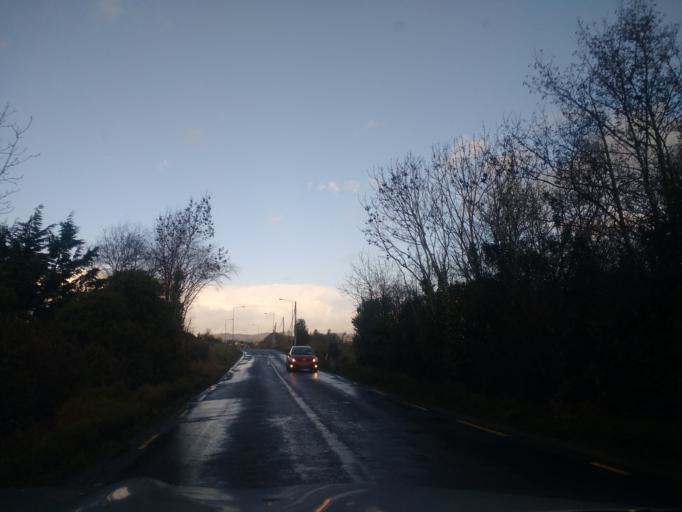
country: IE
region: Ulster
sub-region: County Donegal
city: Ramelton
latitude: 55.0255
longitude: -7.6503
